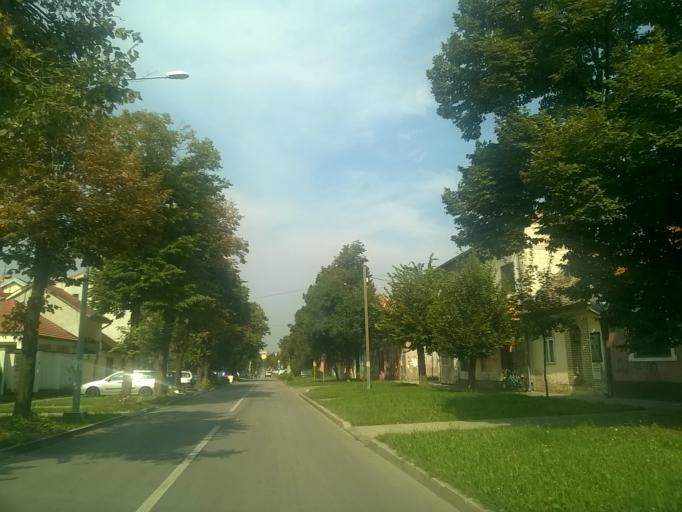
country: RS
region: Autonomna Pokrajina Vojvodina
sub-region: Juznobanatski Okrug
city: Pancevo
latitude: 44.8623
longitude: 20.6504
